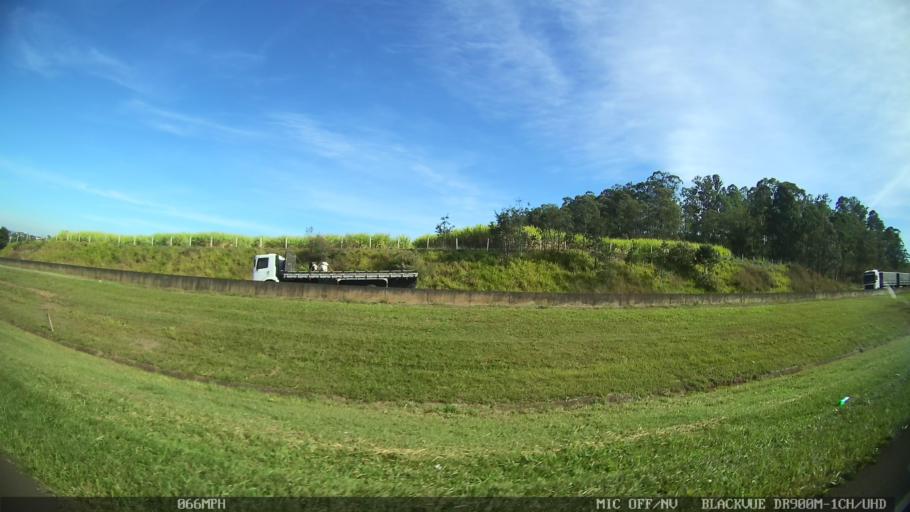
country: BR
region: Sao Paulo
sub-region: Araras
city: Araras
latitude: -22.3342
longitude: -47.3892
